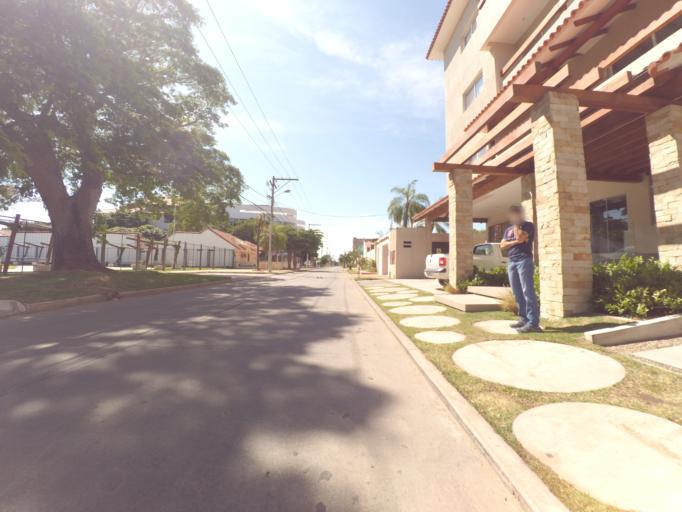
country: BO
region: Santa Cruz
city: Santa Cruz de la Sierra
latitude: -17.8076
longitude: -63.2094
